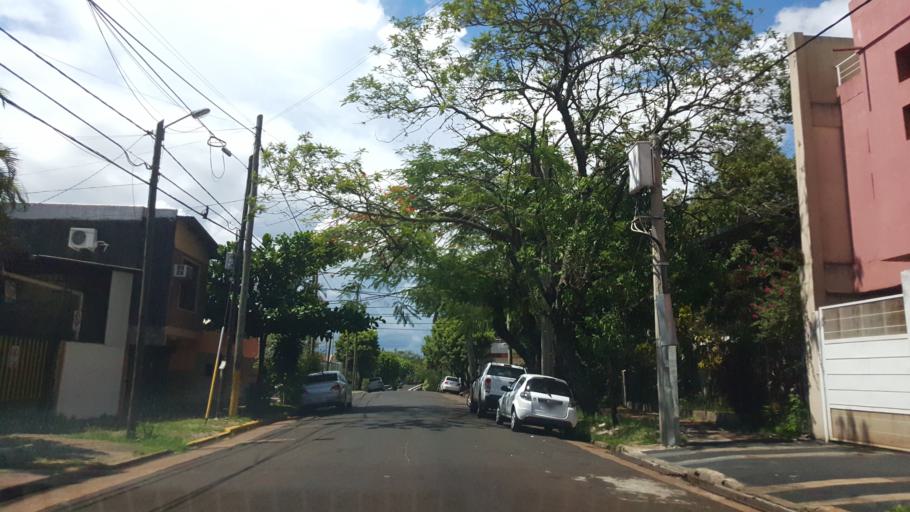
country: AR
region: Misiones
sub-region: Departamento de Capital
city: Posadas
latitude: -27.3563
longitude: -55.8974
